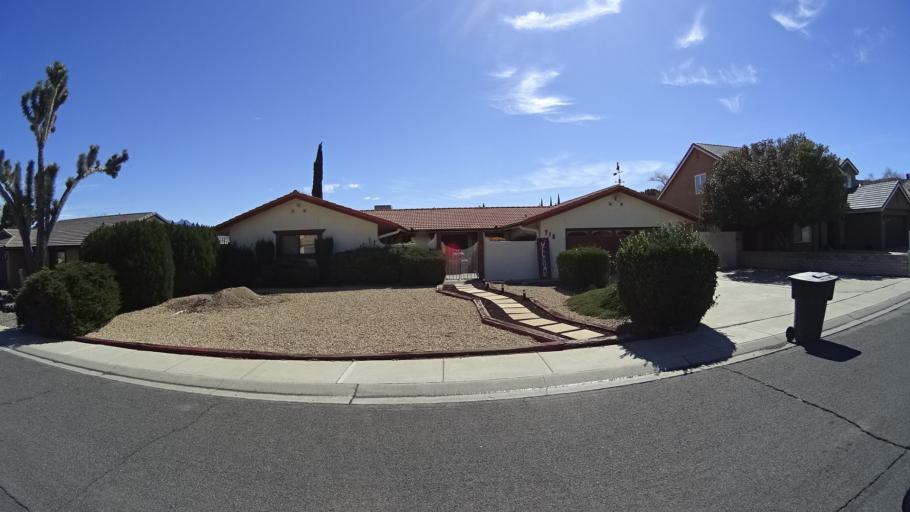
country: US
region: Arizona
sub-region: Mohave County
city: Kingman
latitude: 35.2120
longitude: -114.0496
